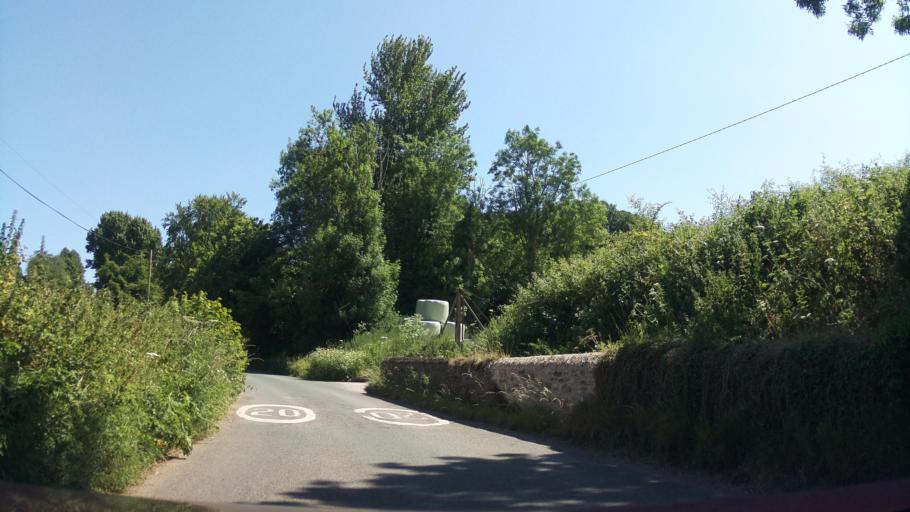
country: GB
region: England
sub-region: Devon
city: Marldon
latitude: 50.4747
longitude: -3.6014
